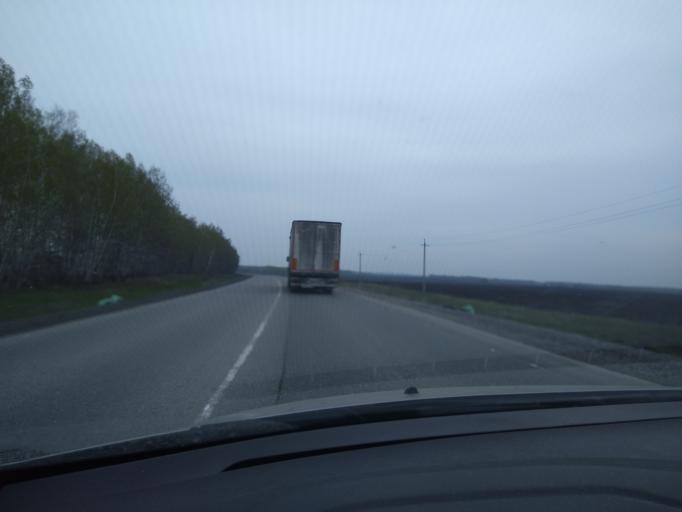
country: RU
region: Sverdlovsk
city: Zarechnyy
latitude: 56.7400
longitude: 61.2384
